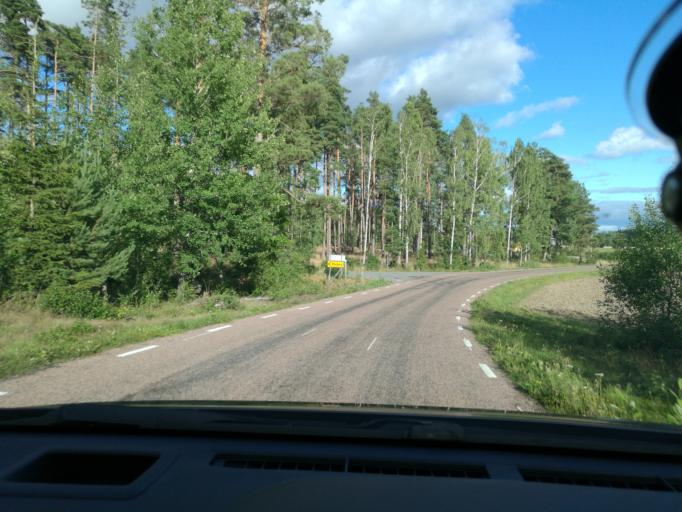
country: SE
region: Vaestmanland
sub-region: Kungsors Kommun
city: Kungsoer
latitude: 59.5466
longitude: 16.1210
